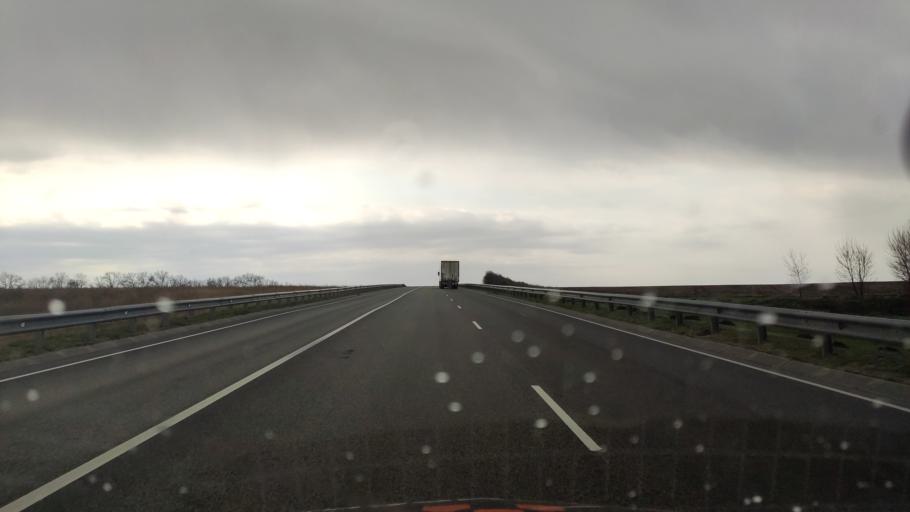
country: RU
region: Voronezj
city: Nizhnedevitsk
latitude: 51.5650
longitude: 38.3569
